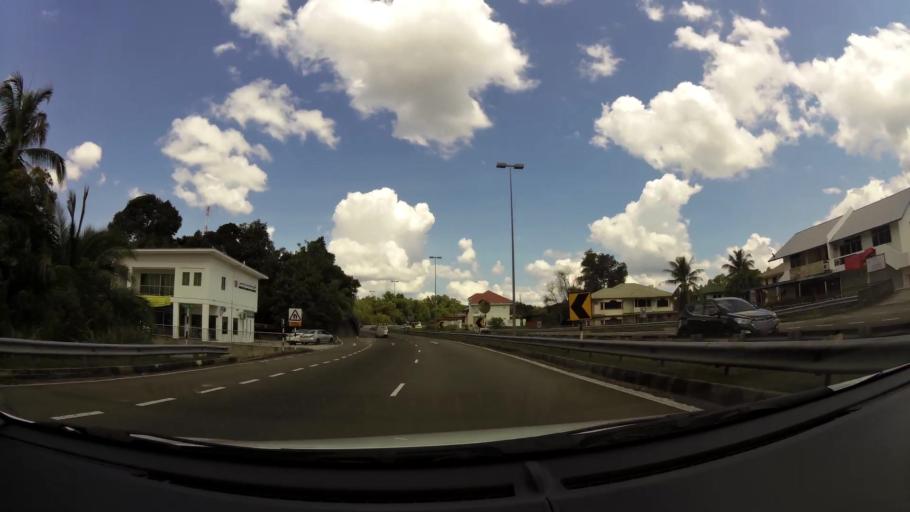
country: BN
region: Brunei and Muara
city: Bandar Seri Begawan
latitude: 4.9411
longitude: 114.9680
